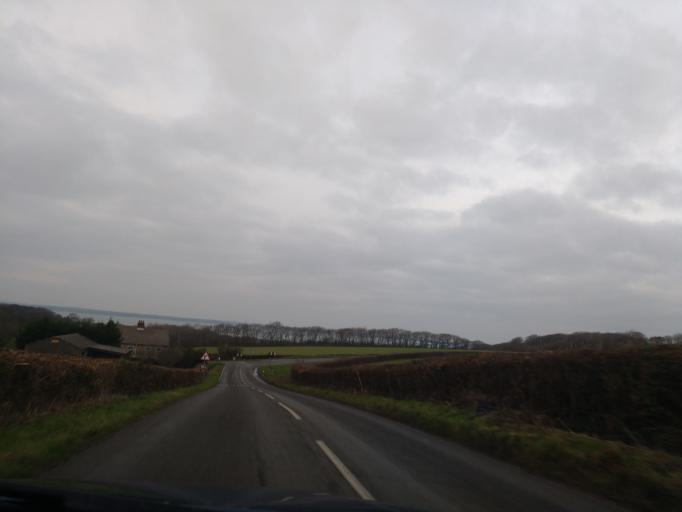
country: GB
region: England
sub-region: Isle of Wight
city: Gurnard
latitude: 50.7292
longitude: -1.3535
